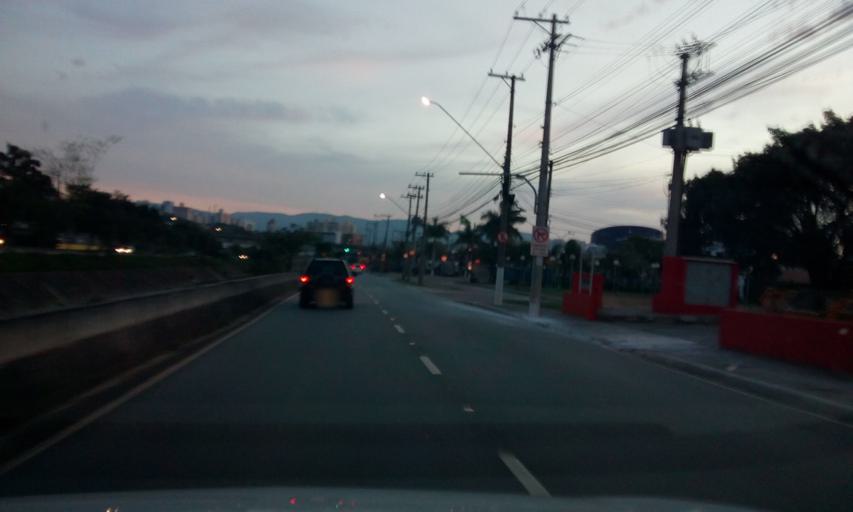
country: BR
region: Sao Paulo
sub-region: Jundiai
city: Jundiai
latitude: -23.1718
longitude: -46.8933
